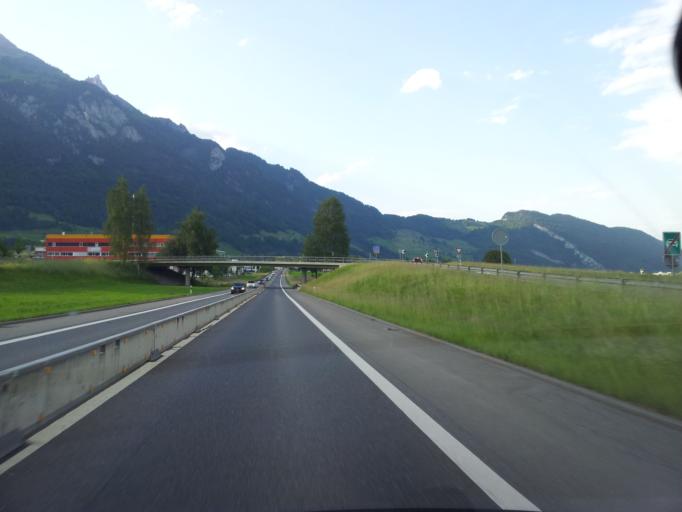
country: CH
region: Obwalden
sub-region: Obwalden
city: Alpnach
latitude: 46.9342
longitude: 8.2773
